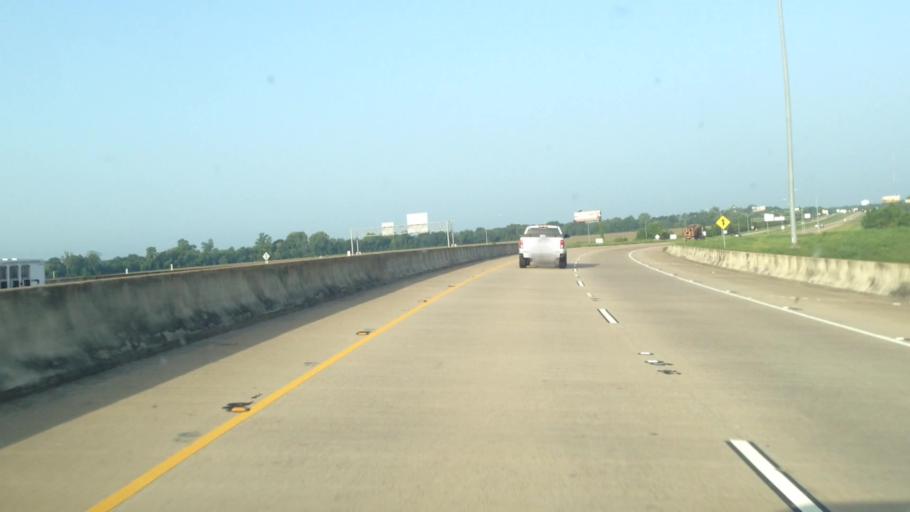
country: US
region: Louisiana
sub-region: Rapides Parish
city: Alexandria
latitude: 31.2416
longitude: -92.4321
